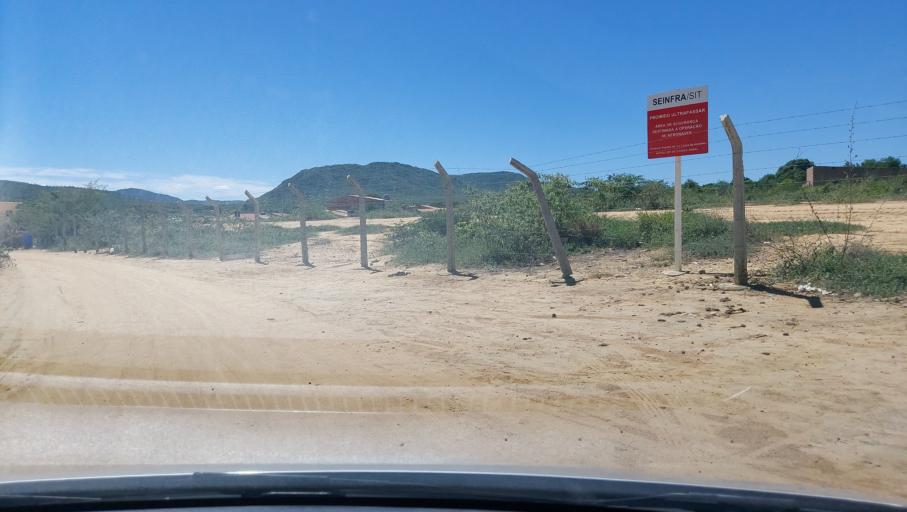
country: BR
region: Bahia
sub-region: Oliveira Dos Brejinhos
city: Beira Rio
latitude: -12.0006
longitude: -42.6307
